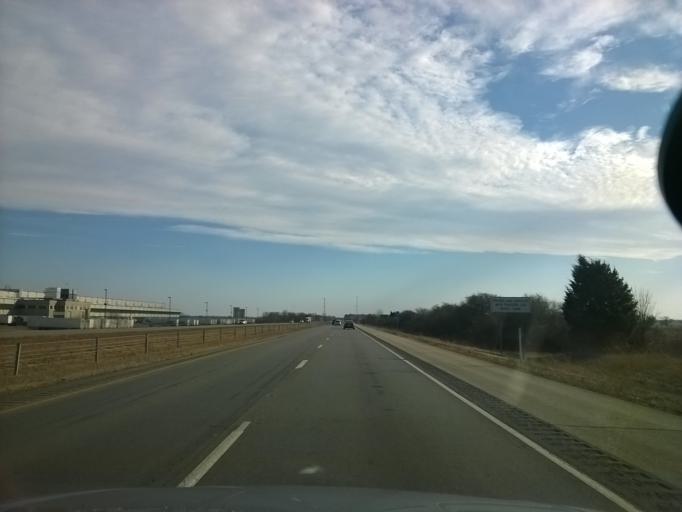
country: US
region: Indiana
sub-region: Johnson County
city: Franklin
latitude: 39.4722
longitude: -86.0100
